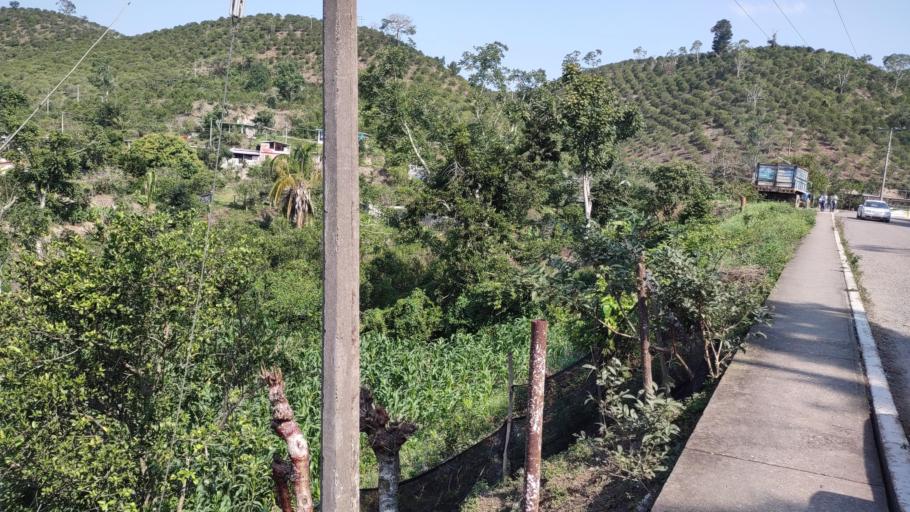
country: MX
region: Veracruz
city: Agua Dulce
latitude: 20.3155
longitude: -97.1739
